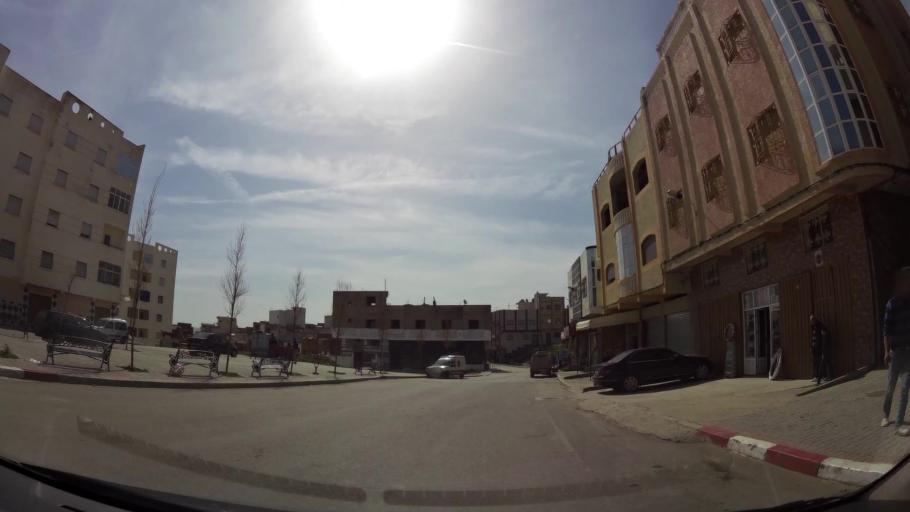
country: MA
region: Tanger-Tetouan
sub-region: Tanger-Assilah
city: Tangier
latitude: 35.7319
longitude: -5.8148
